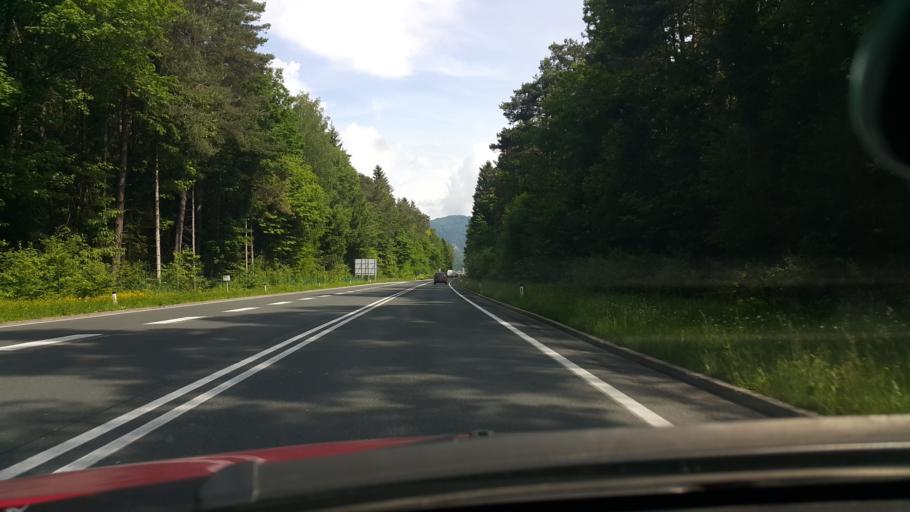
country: SI
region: Trzic
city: Bistrica pri Trzicu
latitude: 46.3181
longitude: 14.2783
